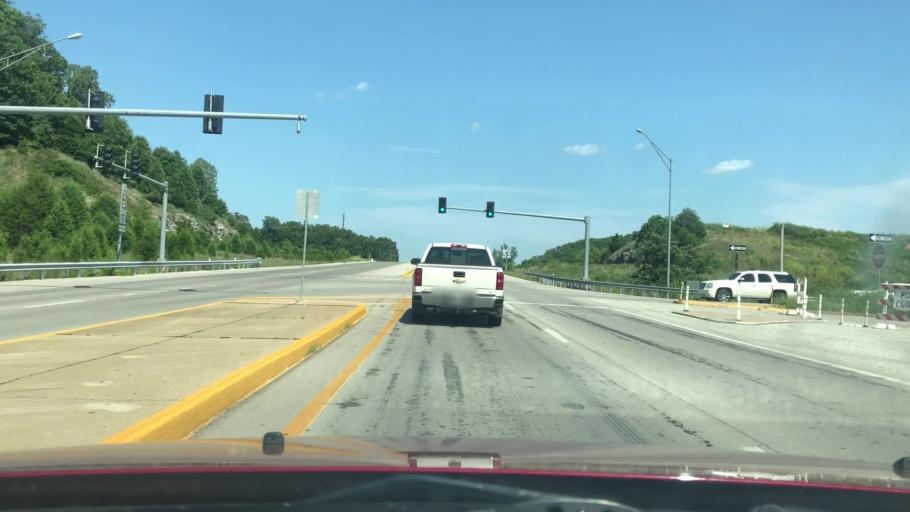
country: US
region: Missouri
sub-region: Stone County
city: Kimberling City
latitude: 36.6757
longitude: -93.3204
